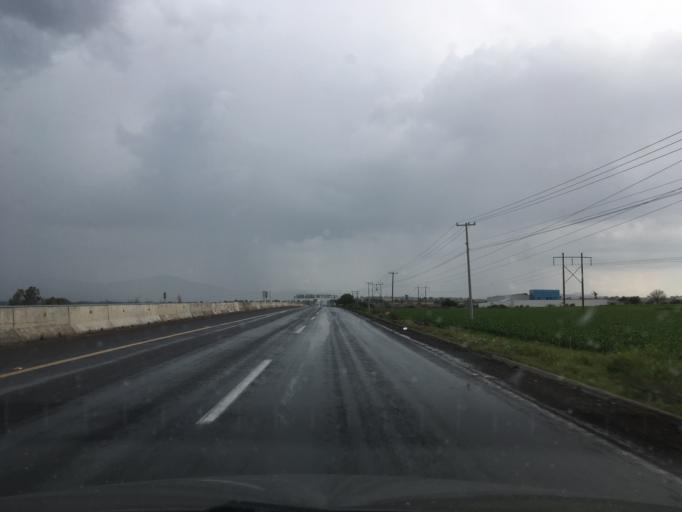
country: MX
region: Guanajuato
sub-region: Tarimoro
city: San Juan Bautista Cacalote
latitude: 20.3394
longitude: -100.8072
